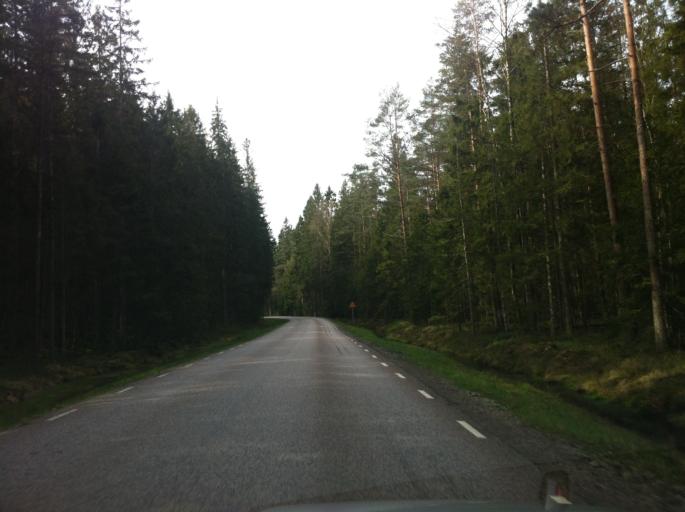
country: SE
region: Vaestra Goetaland
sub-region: Bollebygds Kommun
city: Bollebygd
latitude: 57.5994
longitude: 12.5884
